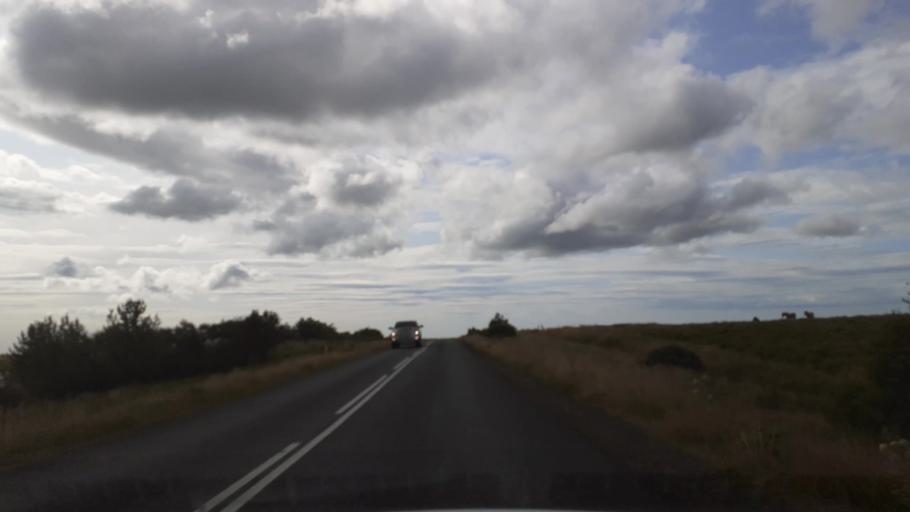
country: IS
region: South
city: Vestmannaeyjar
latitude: 63.8293
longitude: -20.4251
